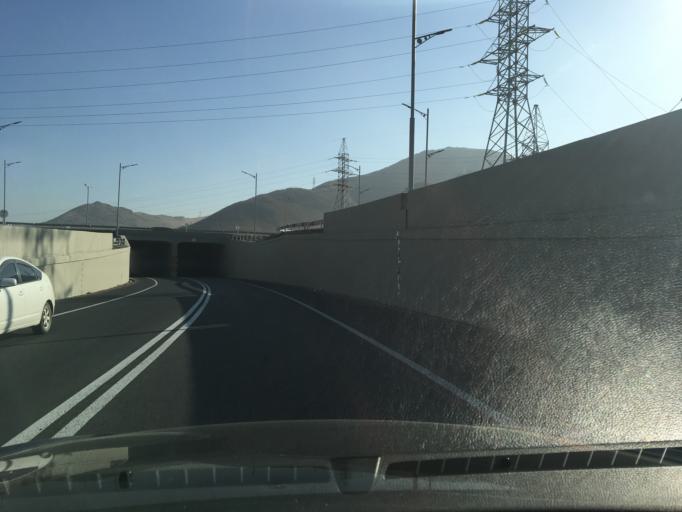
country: MN
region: Ulaanbaatar
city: Ulaanbaatar
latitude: 47.8899
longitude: 106.8627
